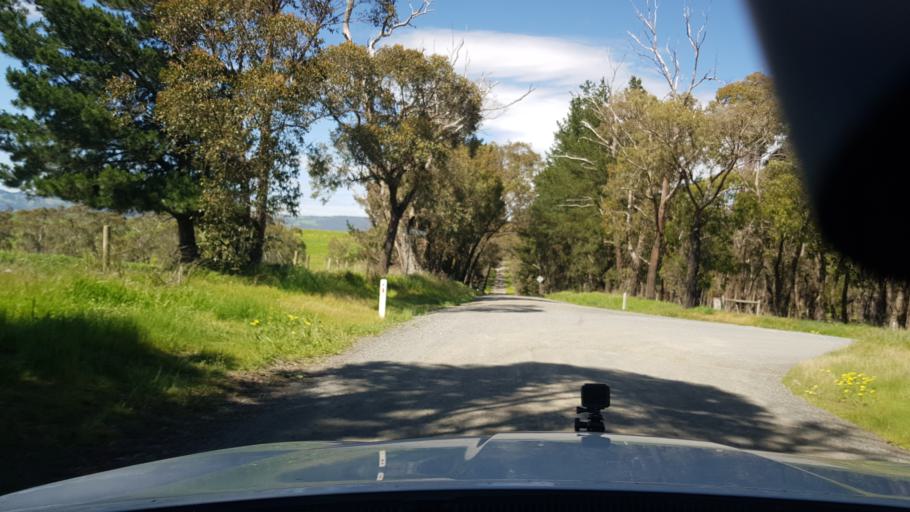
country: AU
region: Victoria
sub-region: Latrobe
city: Moe
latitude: -38.1496
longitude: 146.1373
